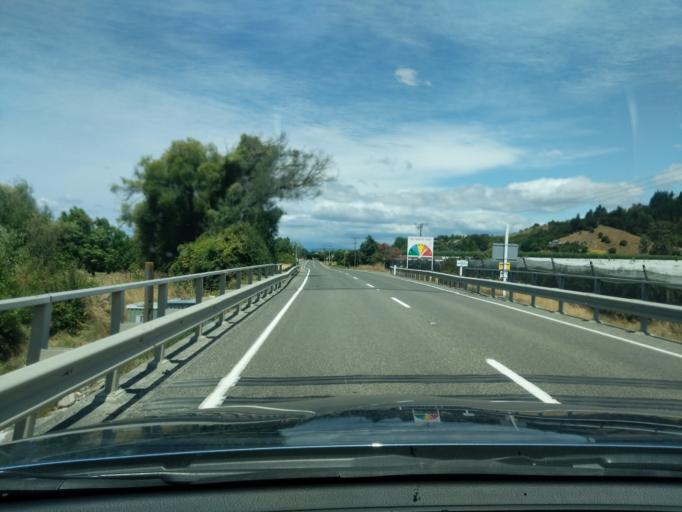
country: NZ
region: Tasman
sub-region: Tasman District
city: Motueka
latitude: -41.0657
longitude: 172.9848
